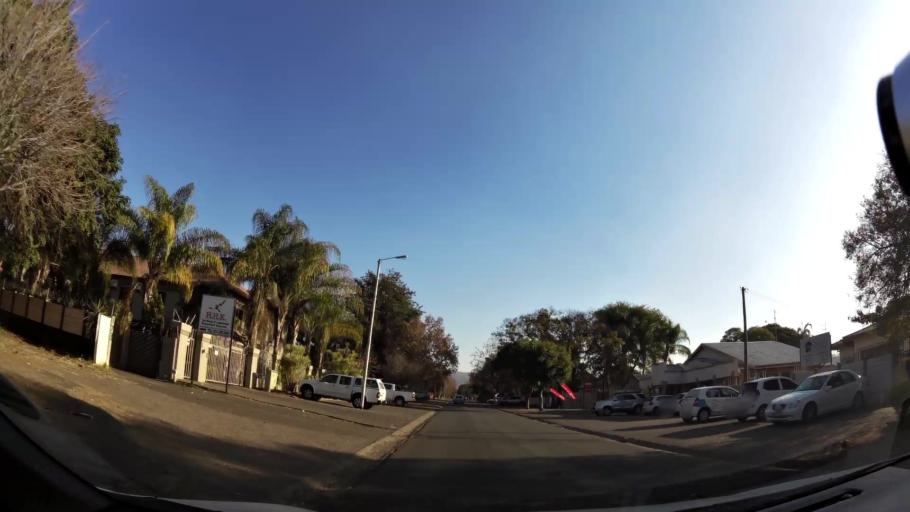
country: ZA
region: North-West
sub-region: Bojanala Platinum District Municipality
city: Rustenburg
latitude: -25.6750
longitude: 27.2375
